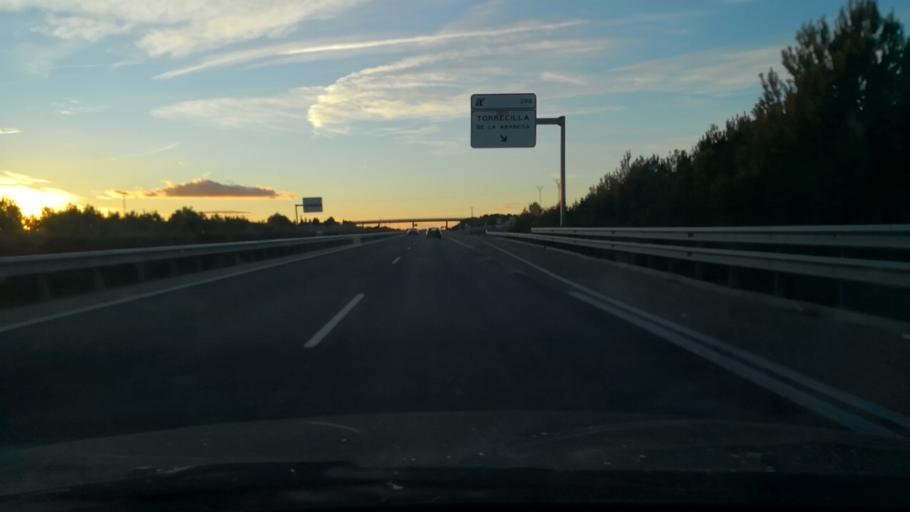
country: ES
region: Castille and Leon
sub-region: Provincia de Valladolid
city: Tordesillas
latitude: 41.5044
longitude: -5.0372
